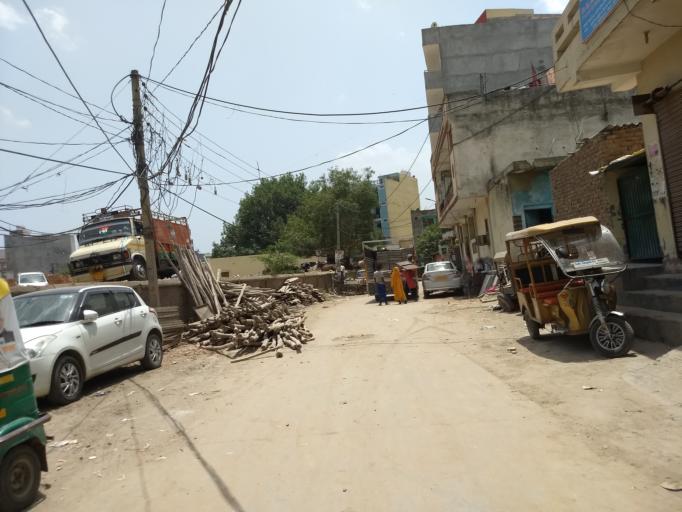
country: IN
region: Haryana
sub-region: Gurgaon
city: Gurgaon
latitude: 28.4895
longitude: 77.1021
